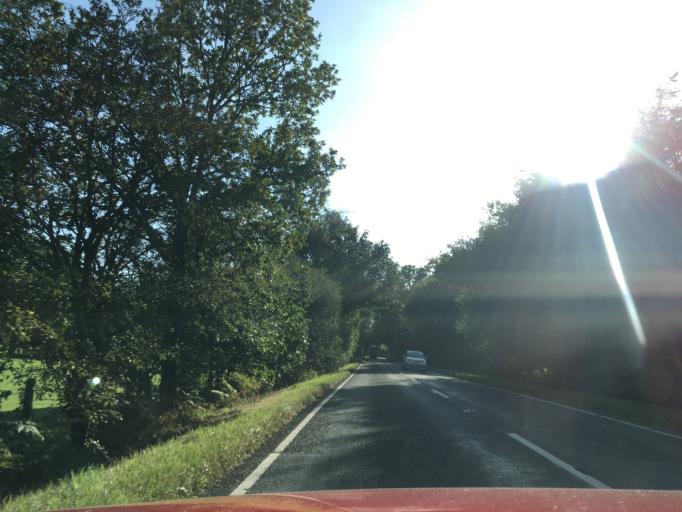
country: GB
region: England
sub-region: Hampshire
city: Four Marks
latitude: 51.0663
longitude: -1.0218
